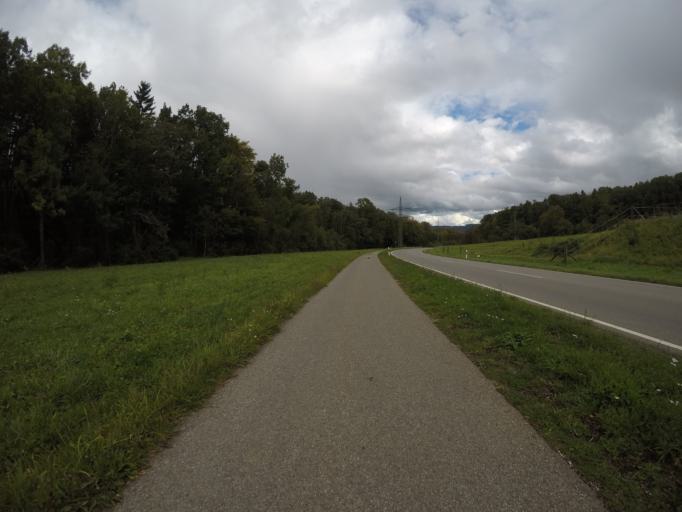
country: DE
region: Baden-Wuerttemberg
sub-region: Tuebingen Region
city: Reutlingen
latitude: 48.4486
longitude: 9.1618
